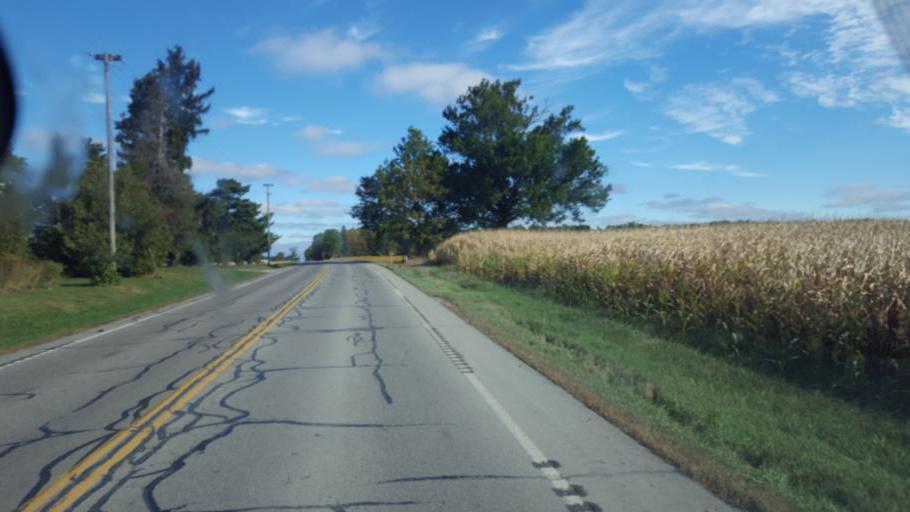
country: US
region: Ohio
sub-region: Huron County
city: Greenwich
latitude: 40.9779
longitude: -82.4914
